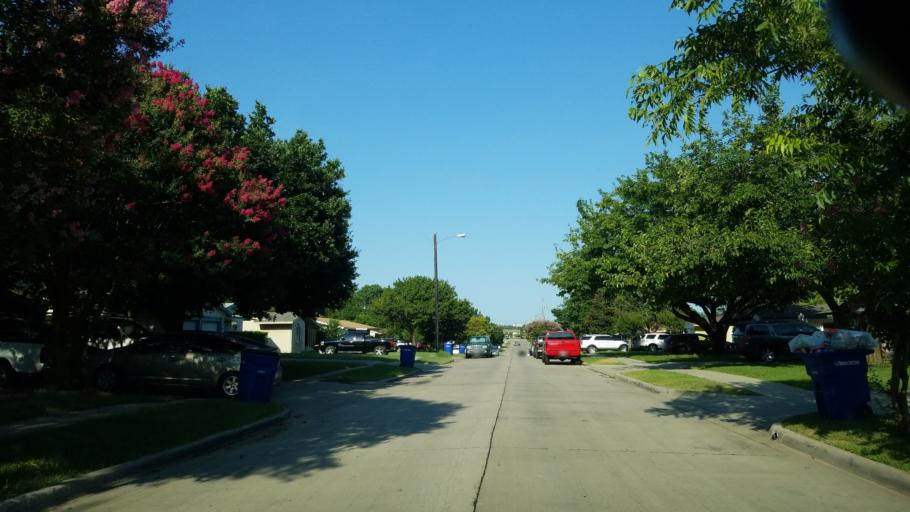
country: US
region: Texas
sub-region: Dallas County
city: Carrollton
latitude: 32.9415
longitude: -96.8942
